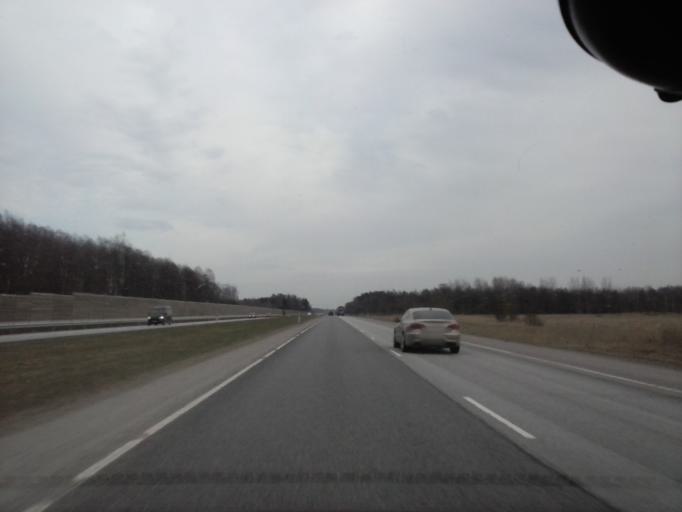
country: EE
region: Harju
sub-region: Rae vald
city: Jueri
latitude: 59.3277
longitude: 24.9173
